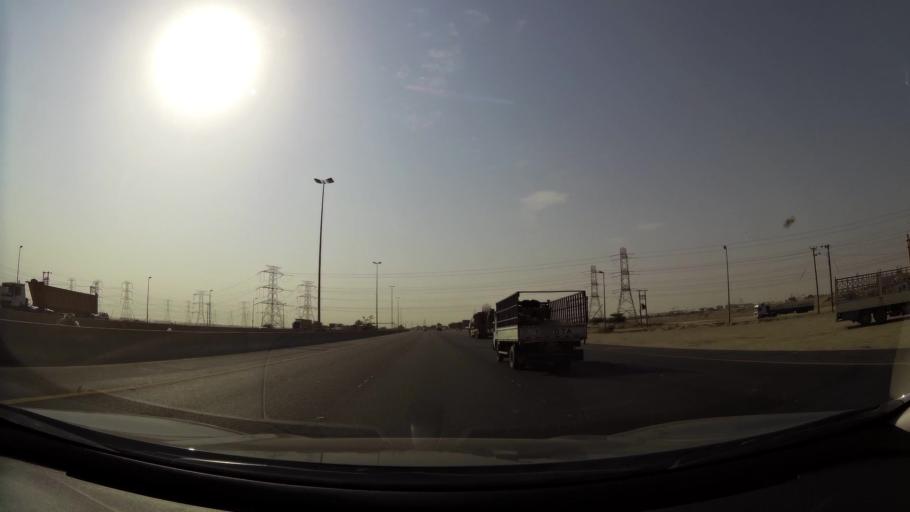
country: KW
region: Al Ahmadi
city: Al Ahmadi
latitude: 29.0063
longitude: 48.0948
